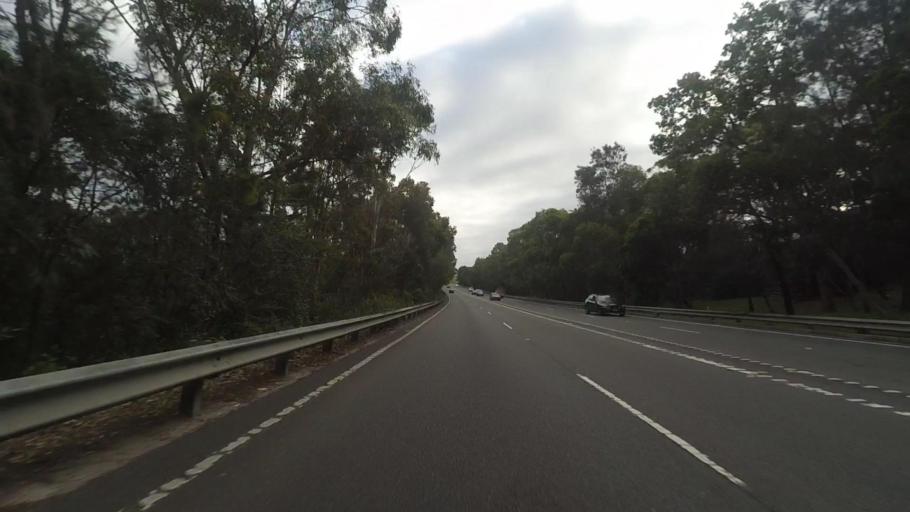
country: AU
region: New South Wales
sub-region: Sutherland Shire
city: Menai
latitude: -34.0072
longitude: 151.0129
